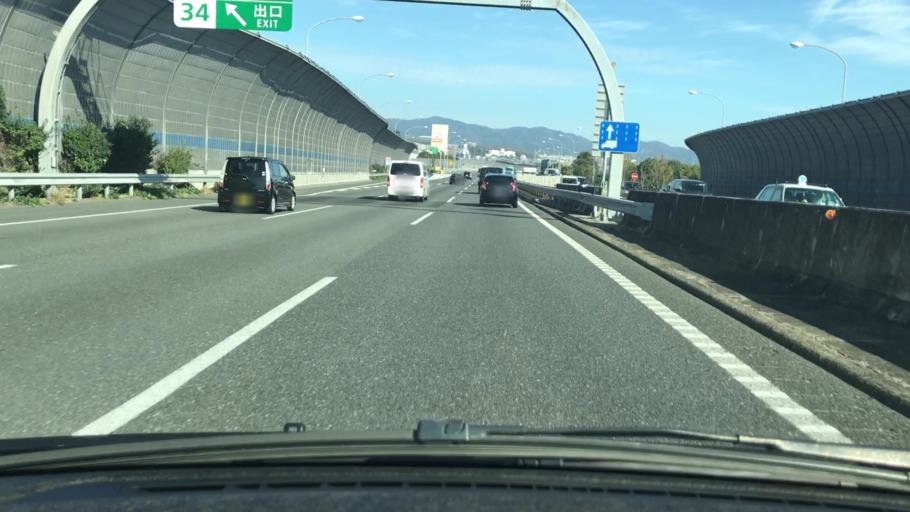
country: JP
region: Osaka
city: Ibaraki
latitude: 34.8279
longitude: 135.5574
